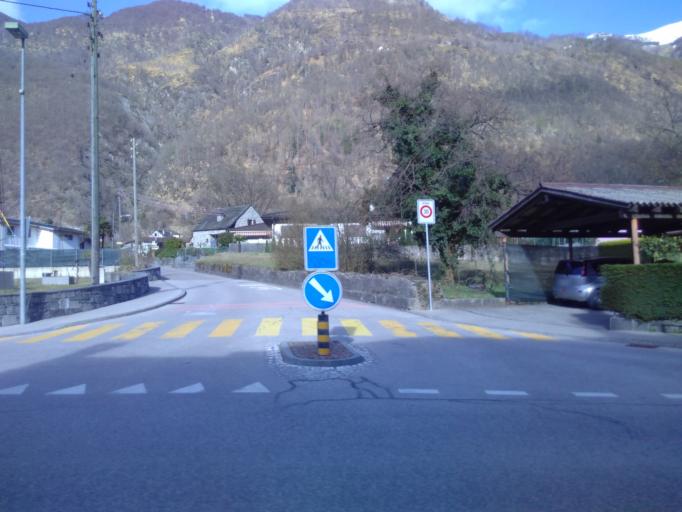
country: CH
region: Ticino
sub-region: Locarno District
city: Verscio
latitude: 46.2255
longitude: 8.7420
